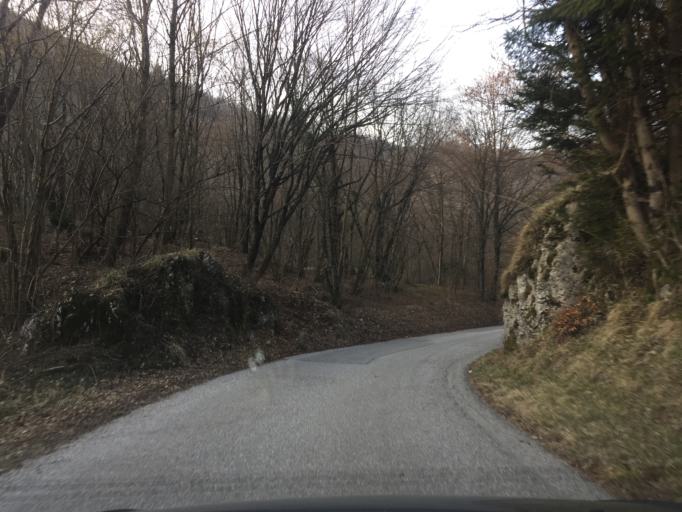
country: SI
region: Kanal
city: Kanal
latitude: 46.0555
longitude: 13.6665
